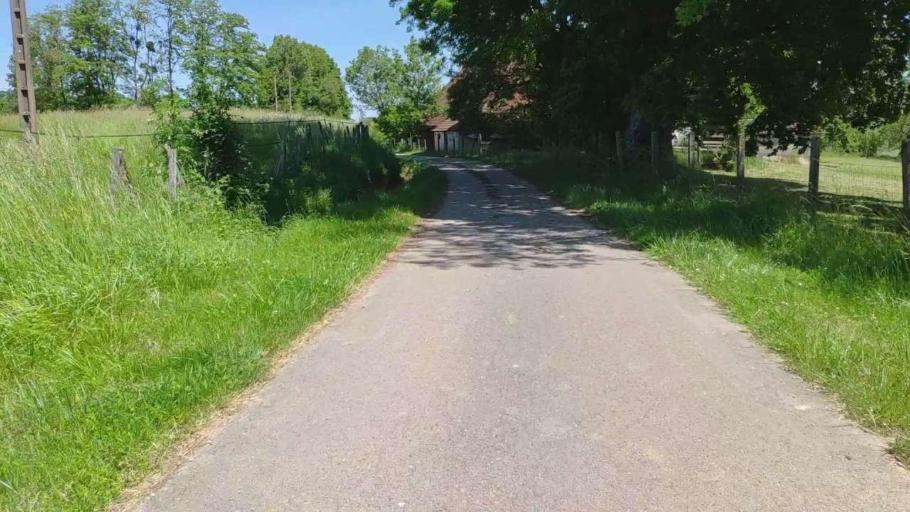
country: FR
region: Franche-Comte
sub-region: Departement du Jura
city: Bletterans
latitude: 46.8000
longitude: 5.3880
